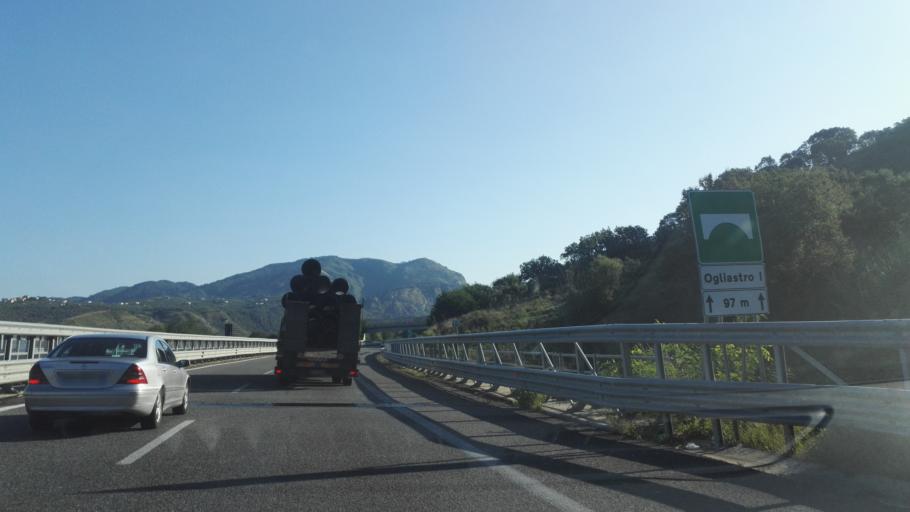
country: IT
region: Calabria
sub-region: Provincia di Catanzaro
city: Nocera Terinese
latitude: 39.0462
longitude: 16.1477
